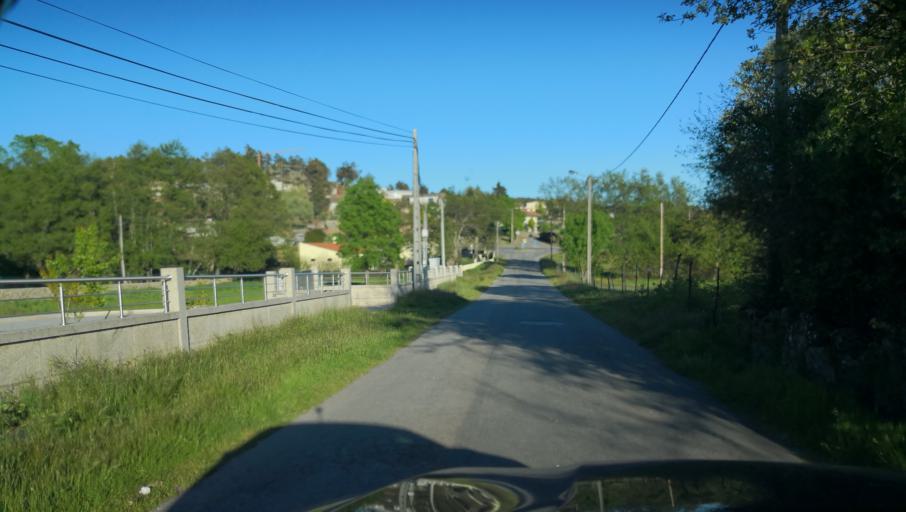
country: PT
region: Vila Real
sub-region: Vila Real
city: Vila Real
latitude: 41.3551
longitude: -7.6477
